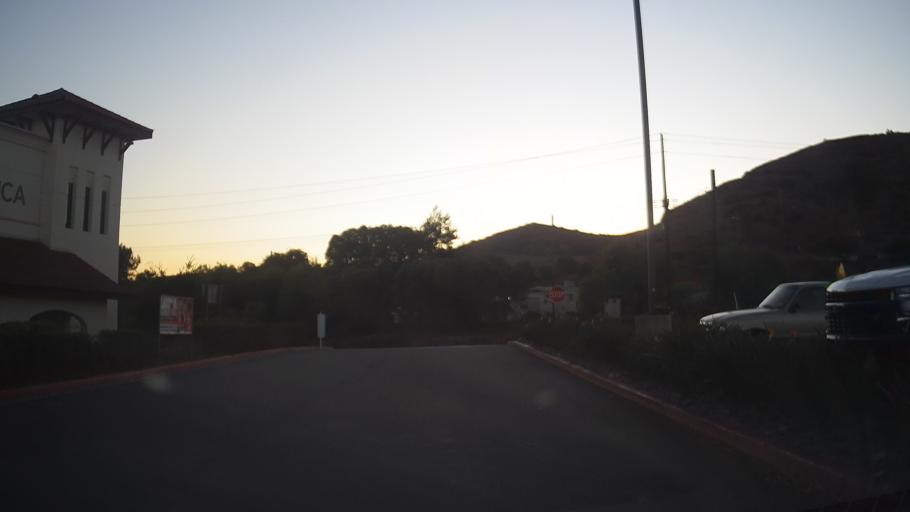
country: US
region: California
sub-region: San Diego County
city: Rancho San Diego
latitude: 32.7365
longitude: -116.9403
